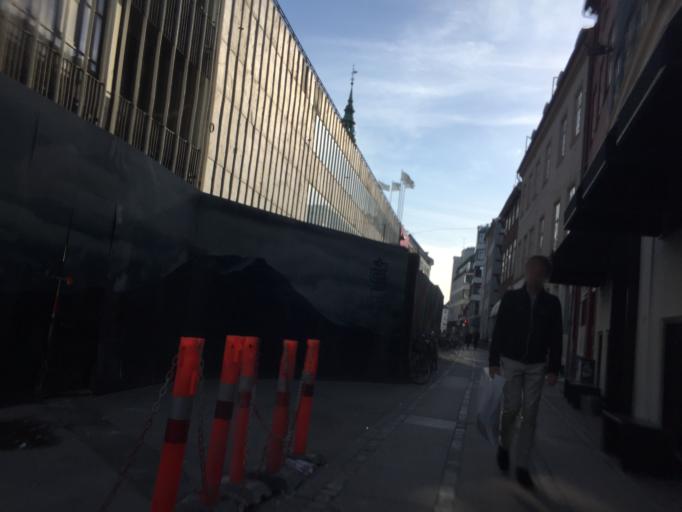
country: DK
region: Capital Region
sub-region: Kobenhavn
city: Christianshavn
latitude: 55.6796
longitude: 12.5841
